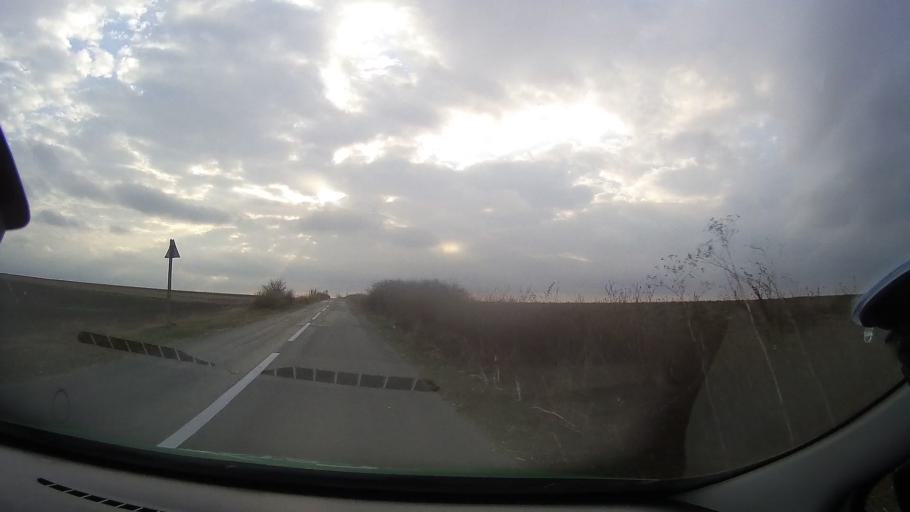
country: RO
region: Constanta
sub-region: Comuna Pestera
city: Pestera
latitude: 44.1325
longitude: 28.1185
